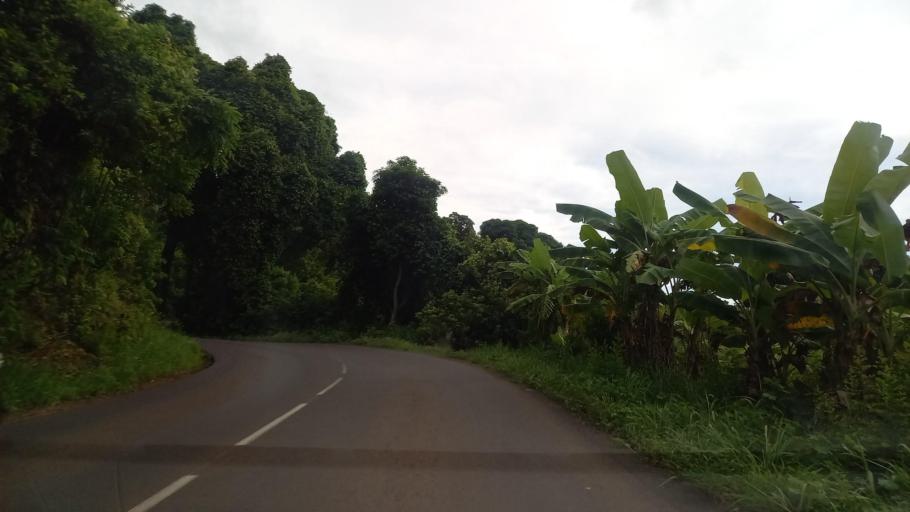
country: YT
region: Bandraboua
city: Bandraboua
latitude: -12.7384
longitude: 45.1178
